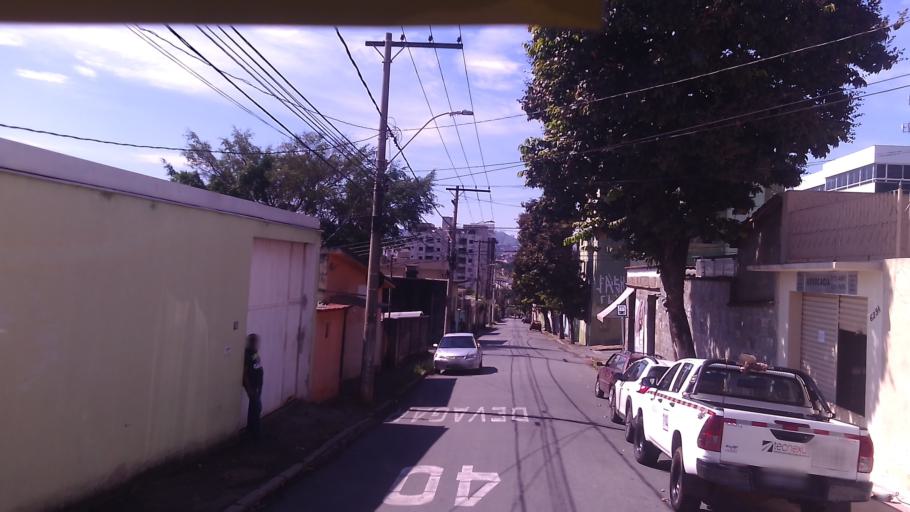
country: BR
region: Minas Gerais
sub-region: Contagem
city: Contagem
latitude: -19.9279
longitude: -43.9980
